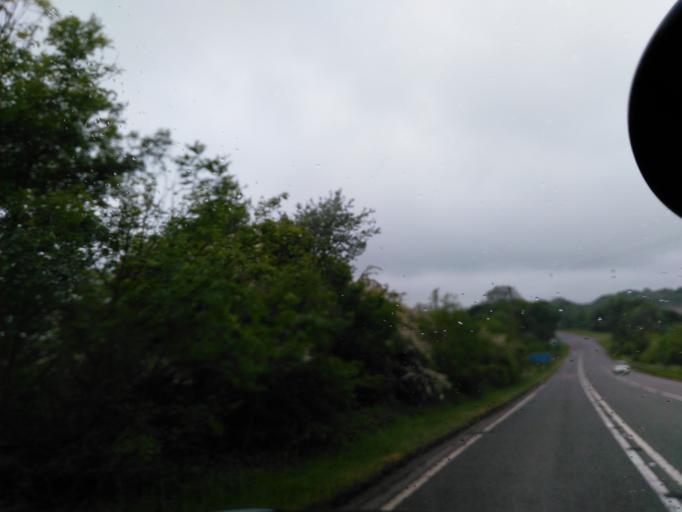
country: GB
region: England
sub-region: Somerset
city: Frome
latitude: 51.2024
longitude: -2.3880
